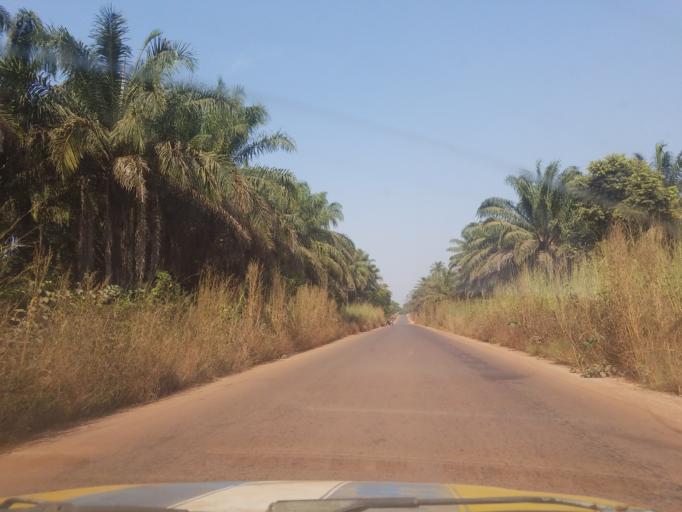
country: GN
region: Boke
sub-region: Boke Prefecture
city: Sangueya
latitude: 10.8265
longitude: -14.3702
